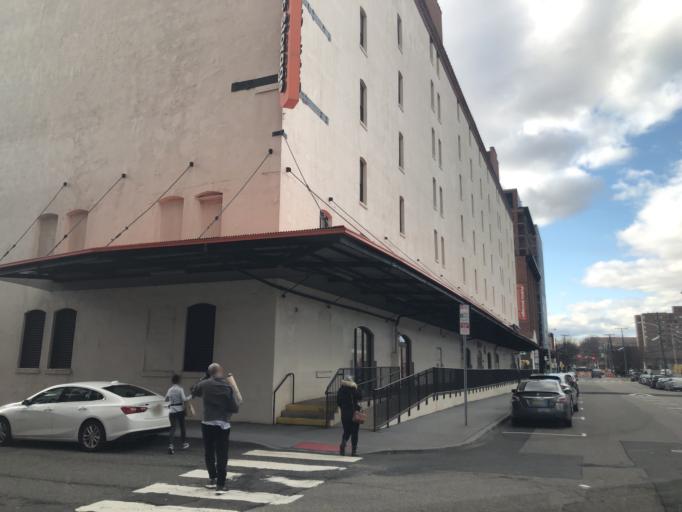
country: US
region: New Jersey
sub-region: Hudson County
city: Hoboken
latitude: 40.7220
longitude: -74.0380
